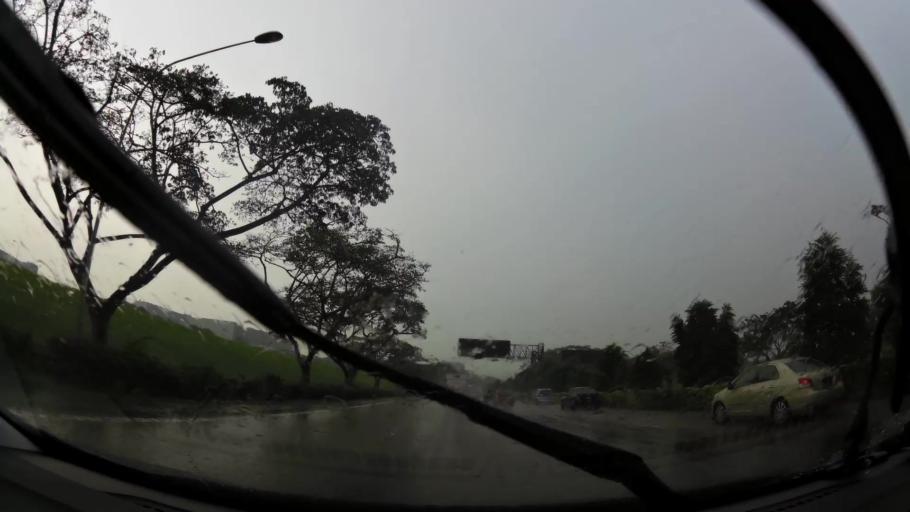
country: MY
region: Johor
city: Kampung Pasir Gudang Baru
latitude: 1.3779
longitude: 103.9256
